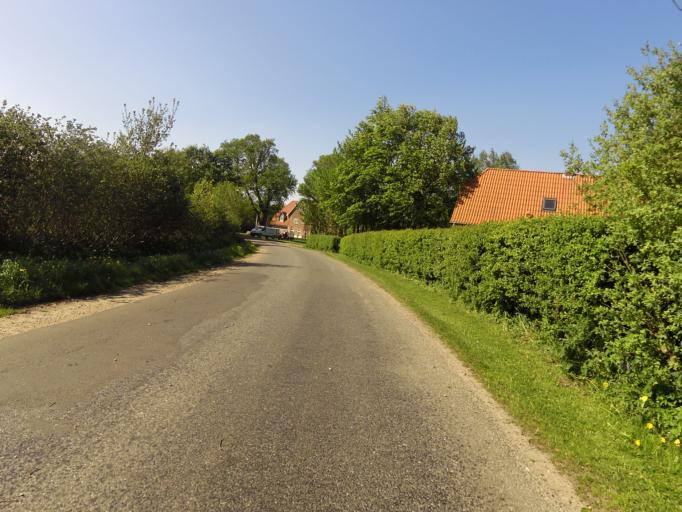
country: DK
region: South Denmark
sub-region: Tonder Kommune
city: Sherrebek
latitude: 55.2199
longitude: 8.8468
